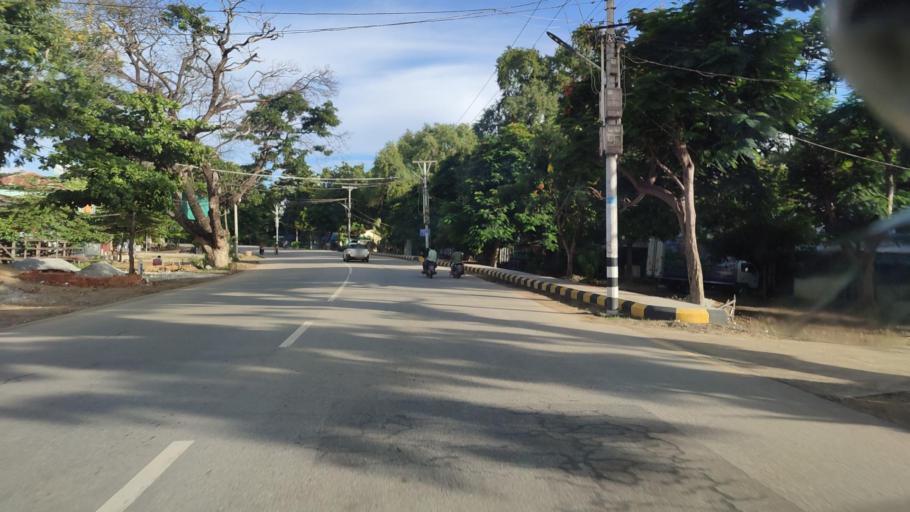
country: MM
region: Mandalay
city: Yamethin
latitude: 20.1364
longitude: 96.1978
